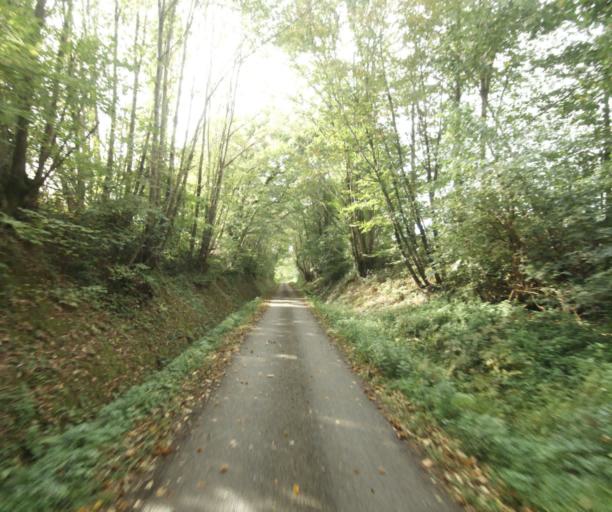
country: FR
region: Midi-Pyrenees
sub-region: Departement du Gers
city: Le Houga
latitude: 43.8787
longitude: -0.1781
